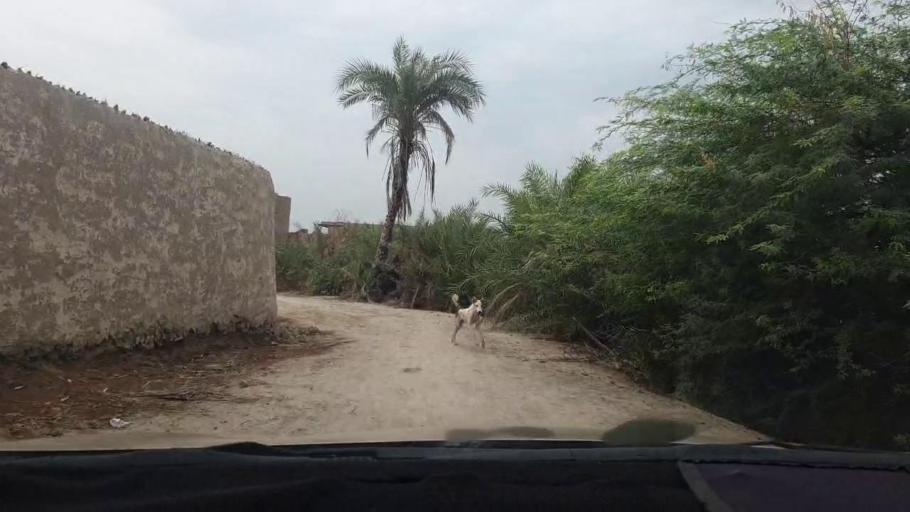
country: PK
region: Sindh
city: Larkana
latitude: 27.5778
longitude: 68.2424
